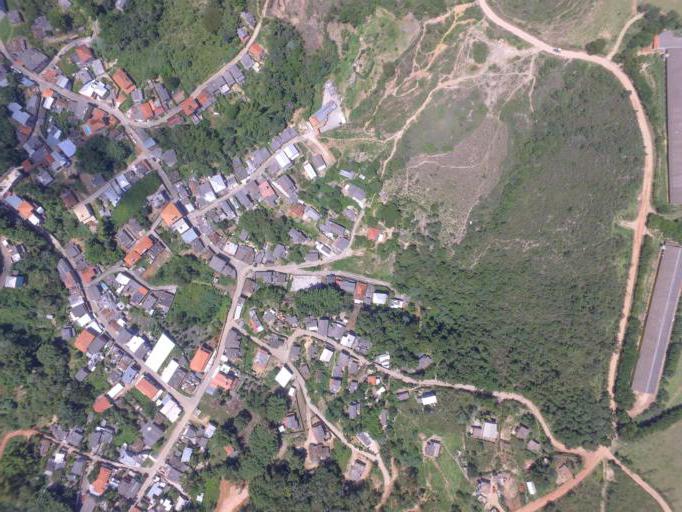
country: BR
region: Minas Gerais
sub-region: Tiradentes
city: Tiradentes
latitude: -21.0523
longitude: -44.0765
